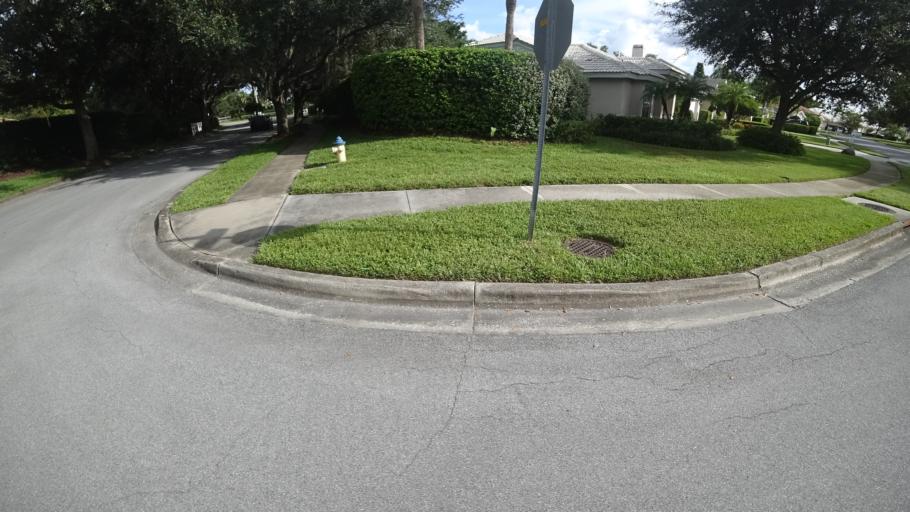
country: US
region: Florida
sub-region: Sarasota County
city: Desoto Lakes
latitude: 27.4154
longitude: -82.4842
